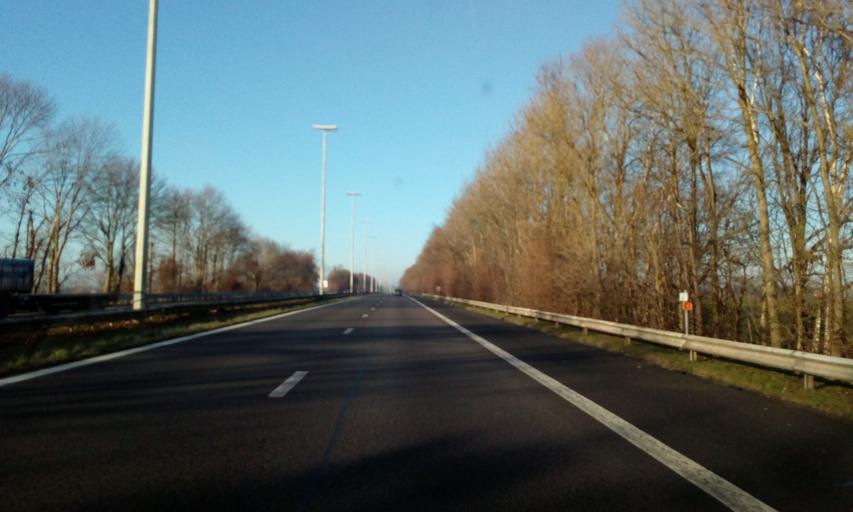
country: BE
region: Wallonia
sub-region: Province du Hainaut
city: Pont-a-Celles
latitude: 50.5354
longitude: 4.3788
